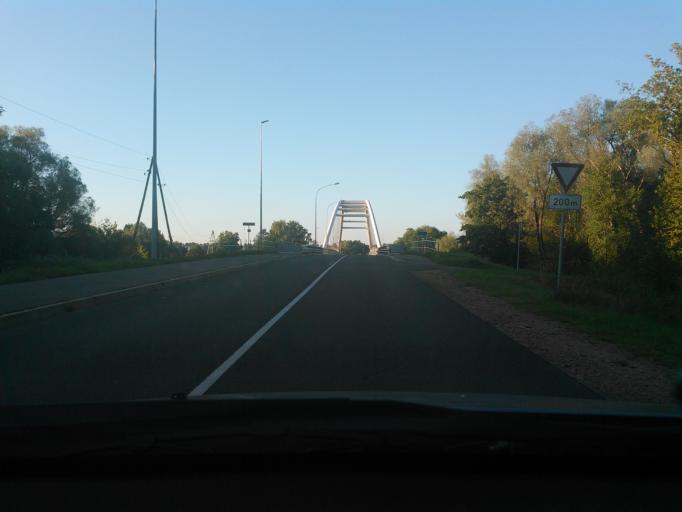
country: LV
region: Adazi
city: Adazi
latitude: 57.0821
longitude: 24.3385
